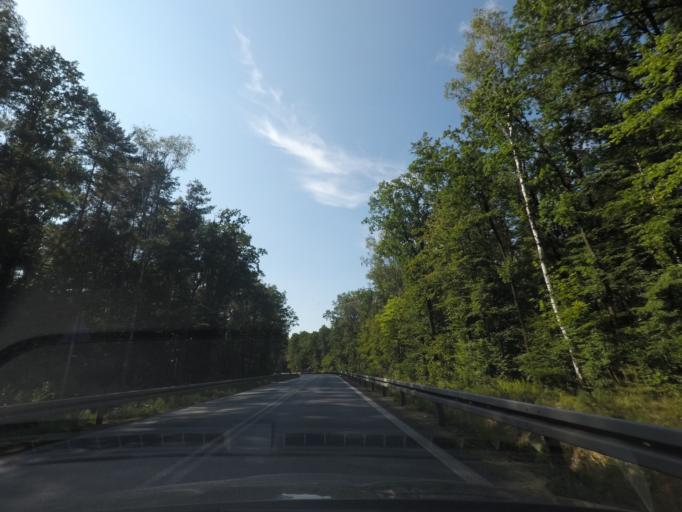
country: PL
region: Silesian Voivodeship
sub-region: Powiat pszczynski
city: Suszec
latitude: 50.0277
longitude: 18.8027
